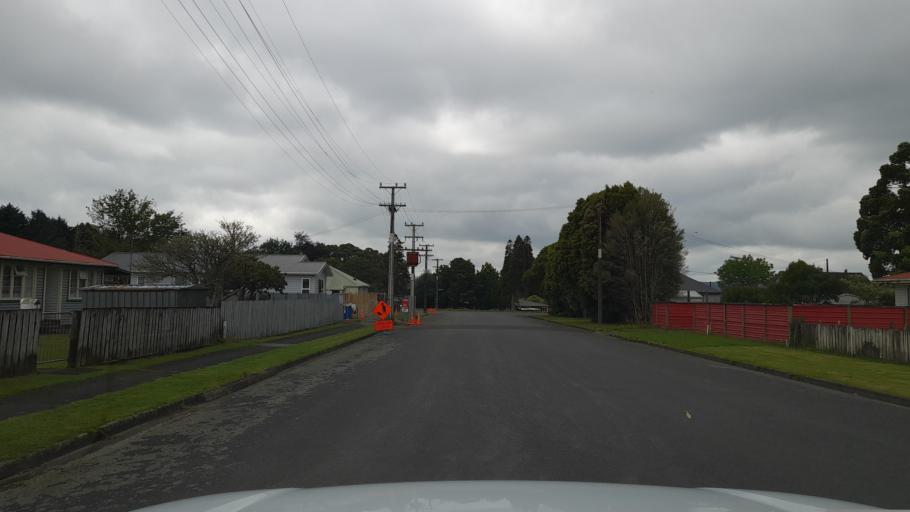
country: NZ
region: Northland
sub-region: Far North District
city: Waimate North
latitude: -35.4038
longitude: 173.7932
